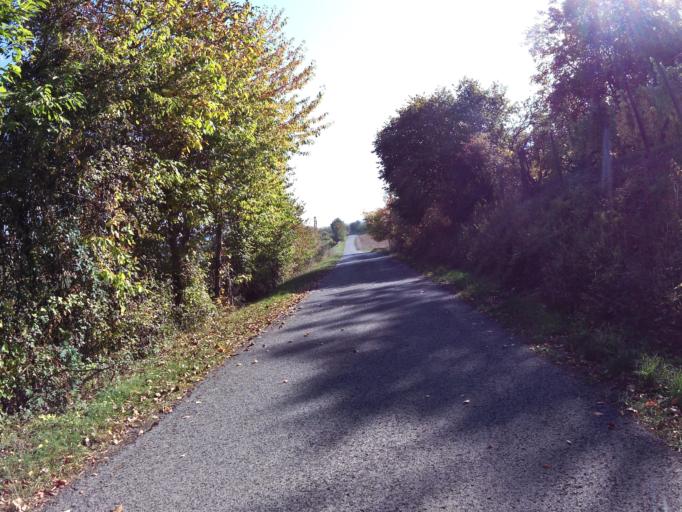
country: DE
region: Bavaria
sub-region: Regierungsbezirk Unterfranken
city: Eibelstadt
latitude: 49.7206
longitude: 9.9921
